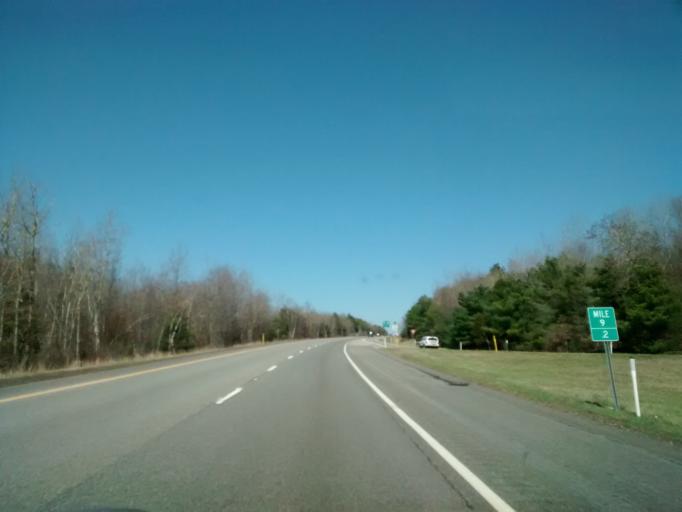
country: US
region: Massachusetts
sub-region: Worcester County
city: Oxford
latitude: 42.1534
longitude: -71.8552
